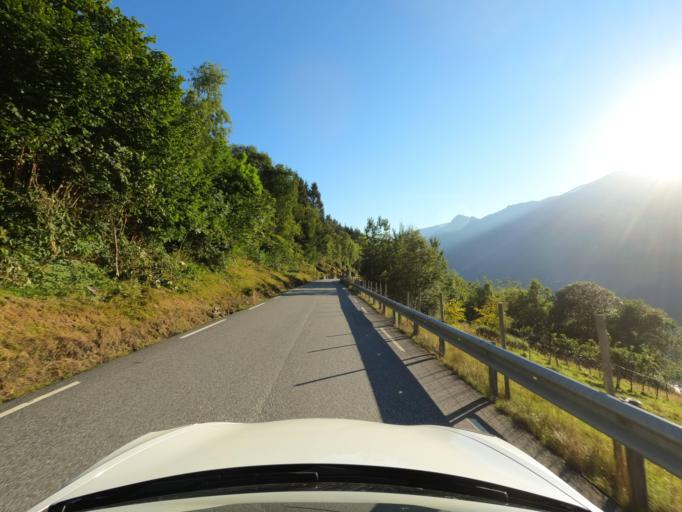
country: NO
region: Hordaland
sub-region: Odda
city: Odda
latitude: 60.2262
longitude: 6.6084
